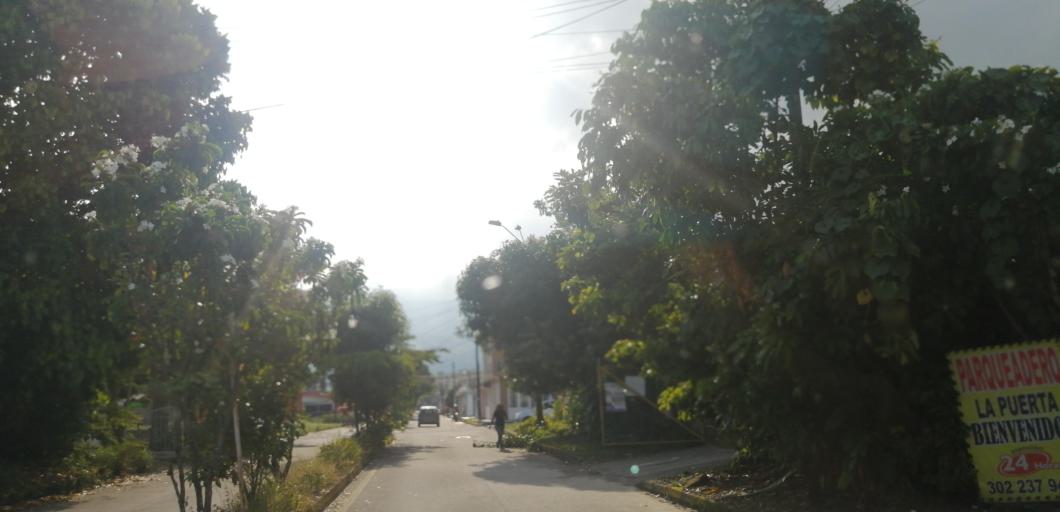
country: CO
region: Meta
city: Acacias
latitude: 3.9863
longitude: -73.7749
